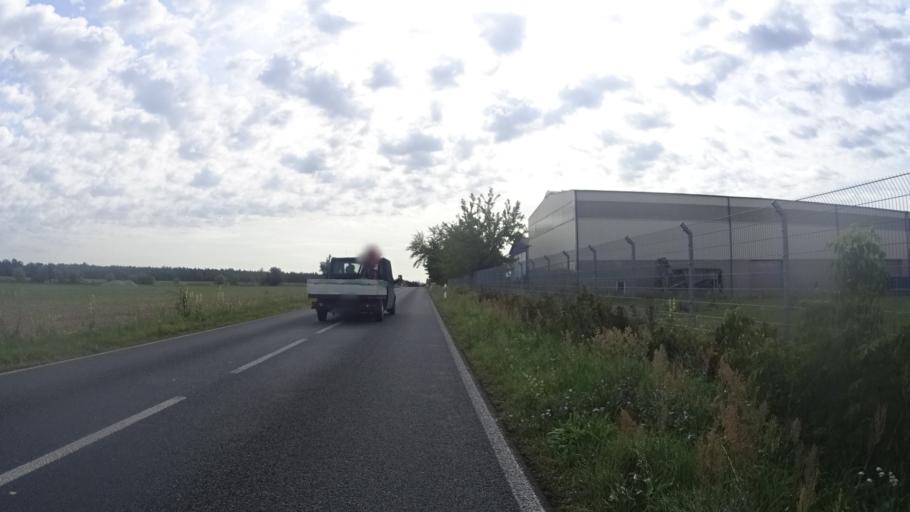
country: DE
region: Brandenburg
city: Brandenburg an der Havel
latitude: 52.3855
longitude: 12.6107
